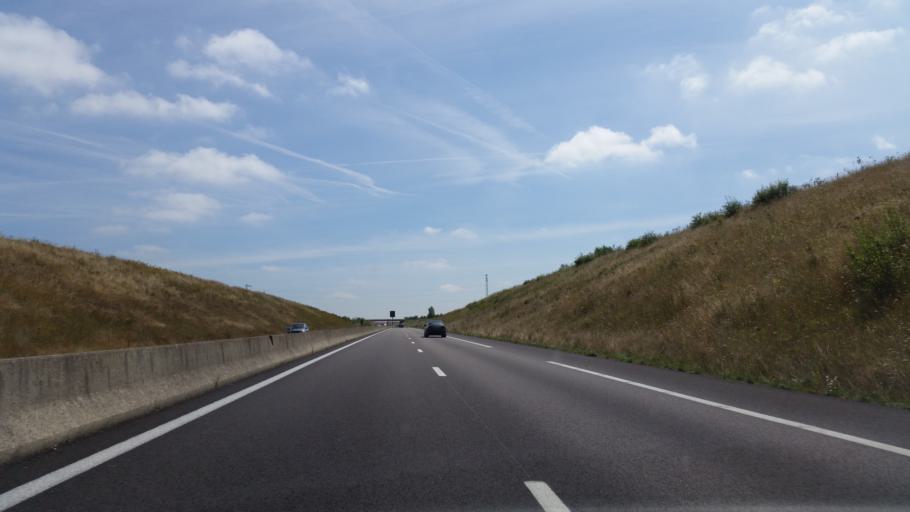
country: FR
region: Haute-Normandie
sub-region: Departement de la Seine-Maritime
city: Gaillefontaine
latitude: 49.7410
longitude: 1.6000
